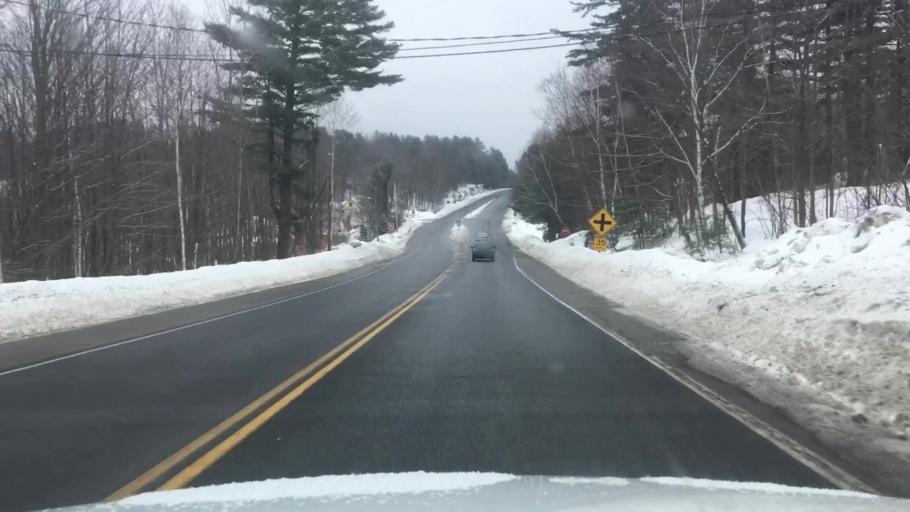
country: US
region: Maine
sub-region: Franklin County
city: Wilton
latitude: 44.5836
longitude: -70.2375
